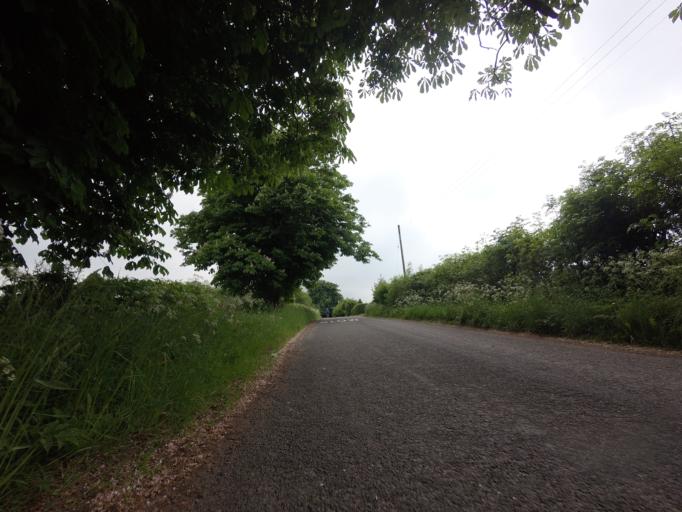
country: GB
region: Scotland
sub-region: Perth and Kinross
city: Kinross
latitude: 56.1843
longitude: -3.4357
